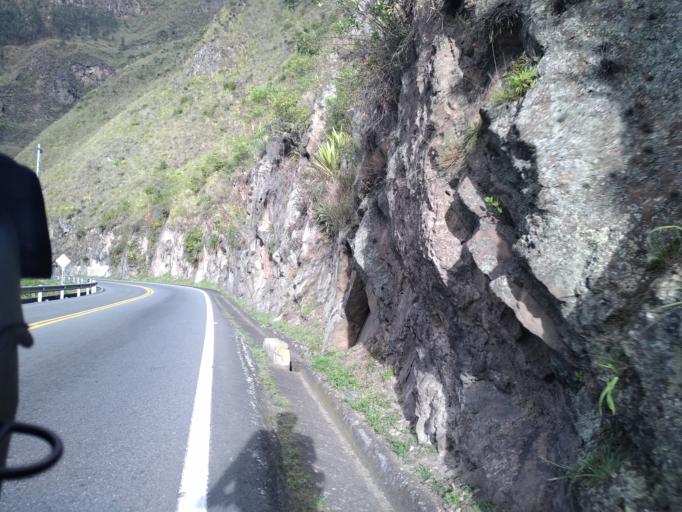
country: CO
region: Narino
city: Funes
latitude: 0.9502
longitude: -77.4721
